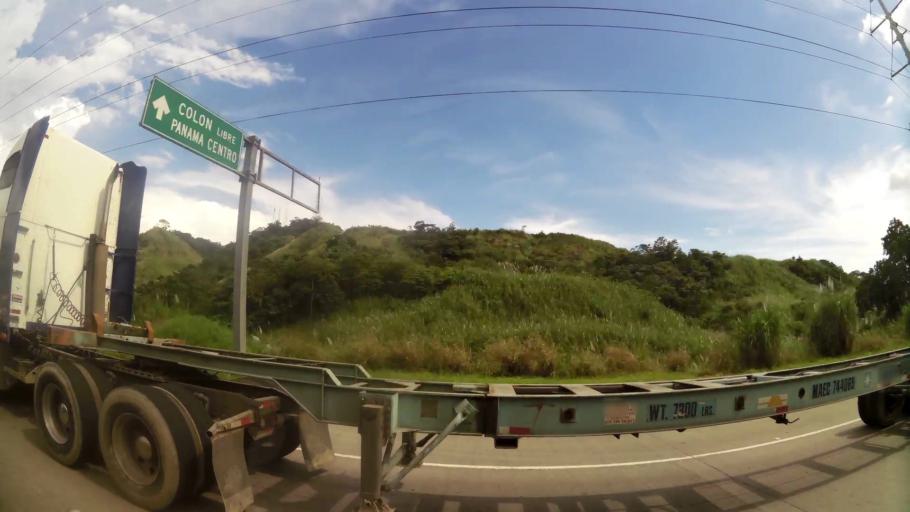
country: PA
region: Panama
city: Las Cumbres
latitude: 9.0508
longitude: -79.5268
